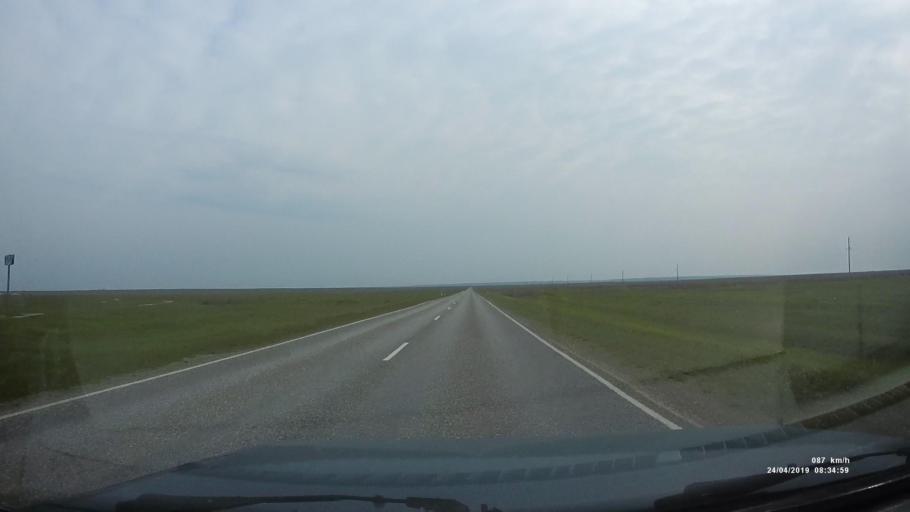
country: RU
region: Kalmykiya
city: Arshan'
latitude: 46.1943
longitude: 43.9126
